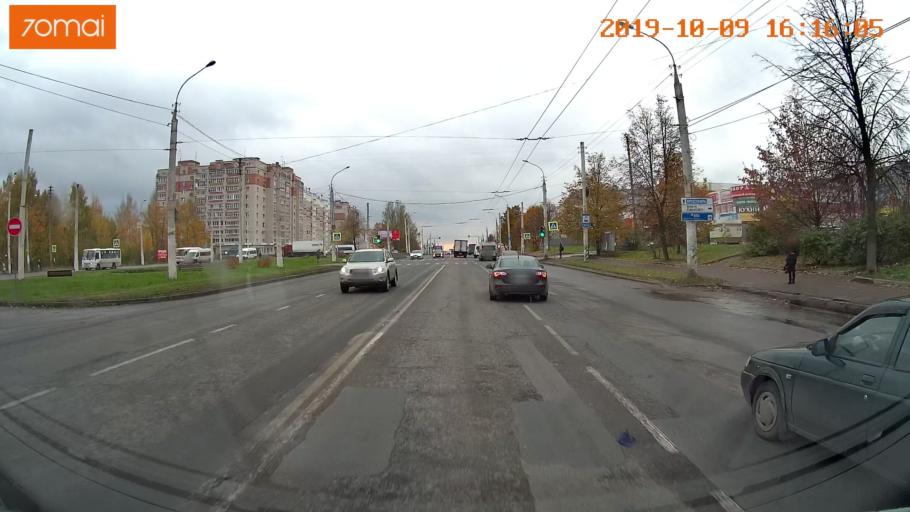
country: RU
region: Kostroma
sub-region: Kostromskoy Rayon
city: Kostroma
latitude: 57.7367
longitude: 40.9114
